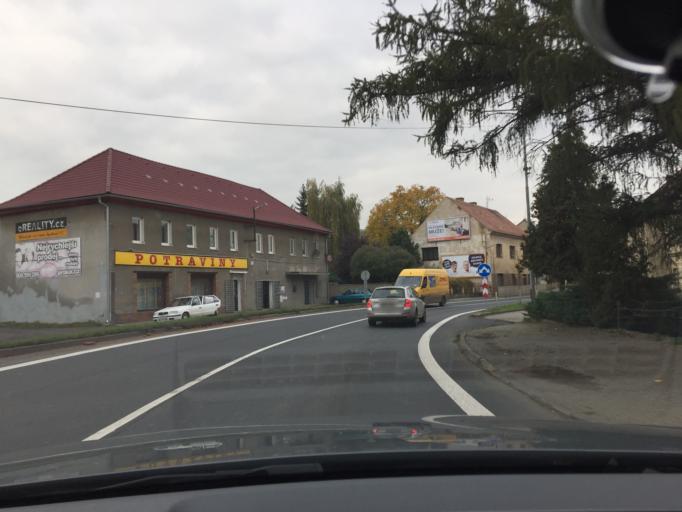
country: CZ
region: Ustecky
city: Velemin
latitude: 50.5388
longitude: 13.9773
